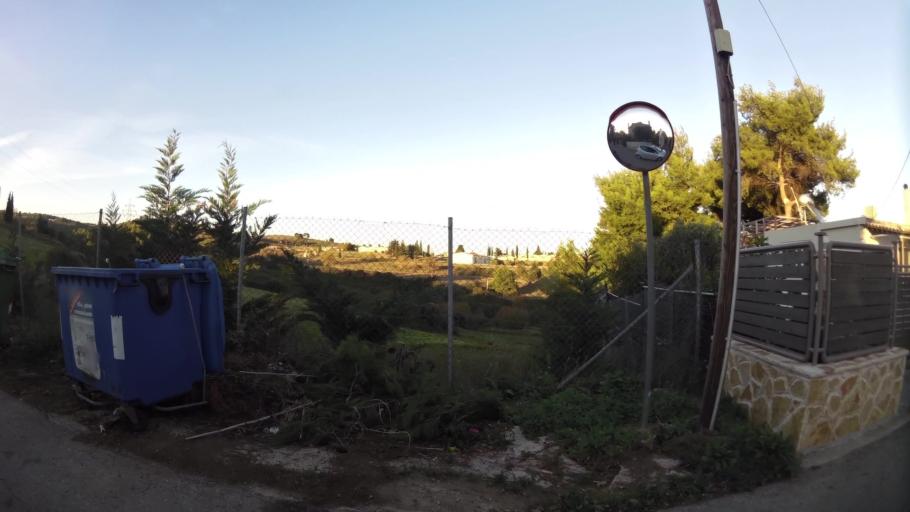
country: GR
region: Attica
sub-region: Nomarchia Anatolikis Attikis
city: Kryoneri
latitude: 38.1476
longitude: 23.8404
